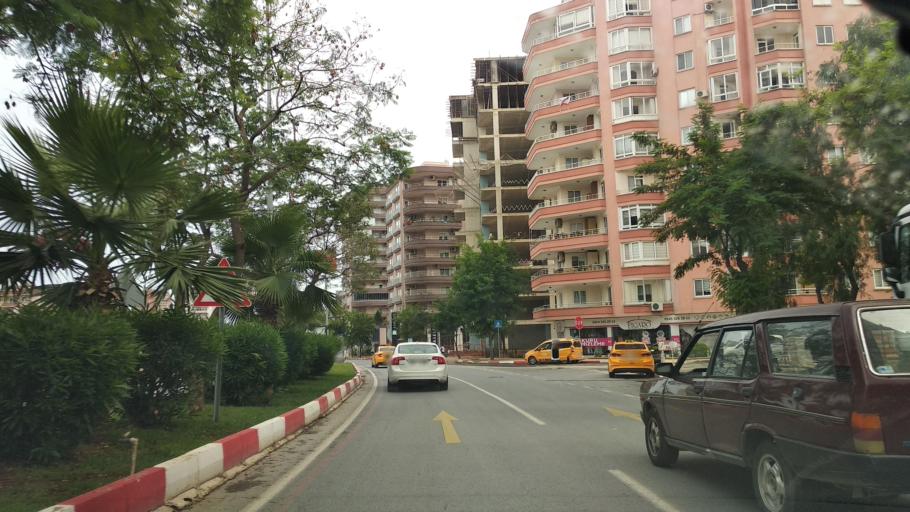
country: TR
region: Mersin
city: Mercin
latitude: 36.7974
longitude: 34.5956
